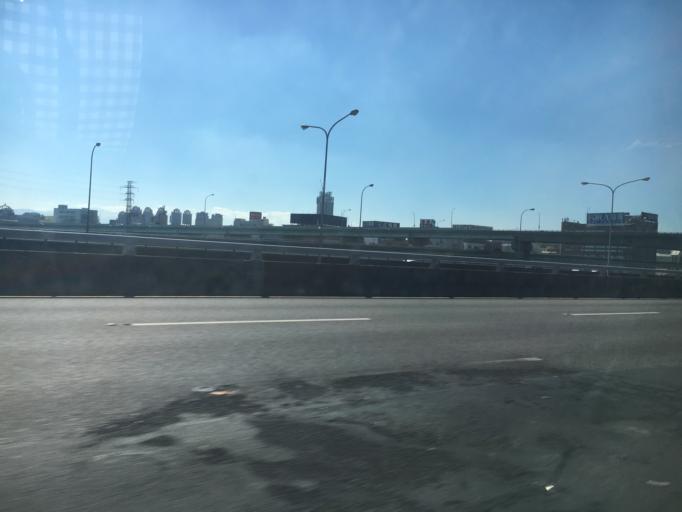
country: TW
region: Taipei
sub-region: Taipei
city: Banqiao
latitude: 25.0743
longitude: 121.4564
